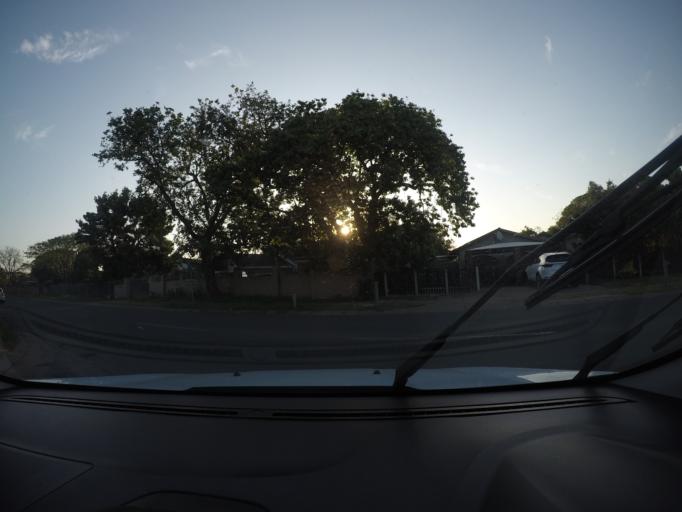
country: ZA
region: KwaZulu-Natal
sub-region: uThungulu District Municipality
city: Richards Bay
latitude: -28.7811
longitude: 32.0996
